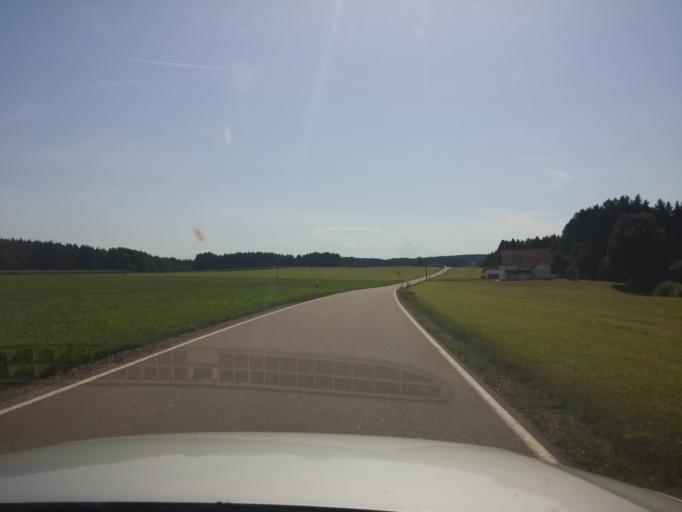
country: DE
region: Baden-Wuerttemberg
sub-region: Tuebingen Region
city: Aichstetten
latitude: 47.8695
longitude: 10.0965
